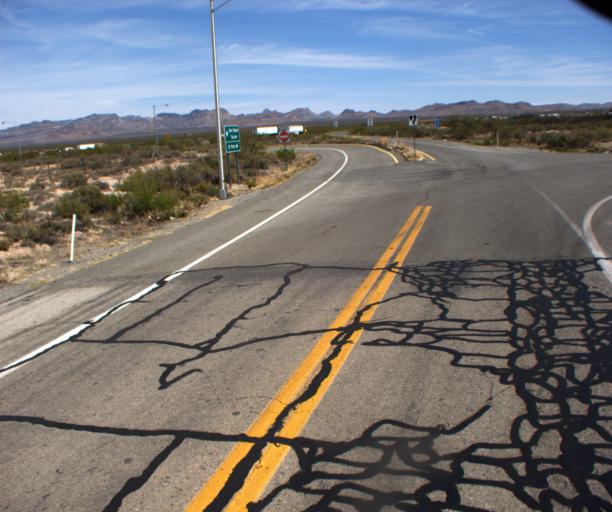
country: US
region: New Mexico
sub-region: Hidalgo County
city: Lordsburg
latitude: 32.2560
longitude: -109.1925
